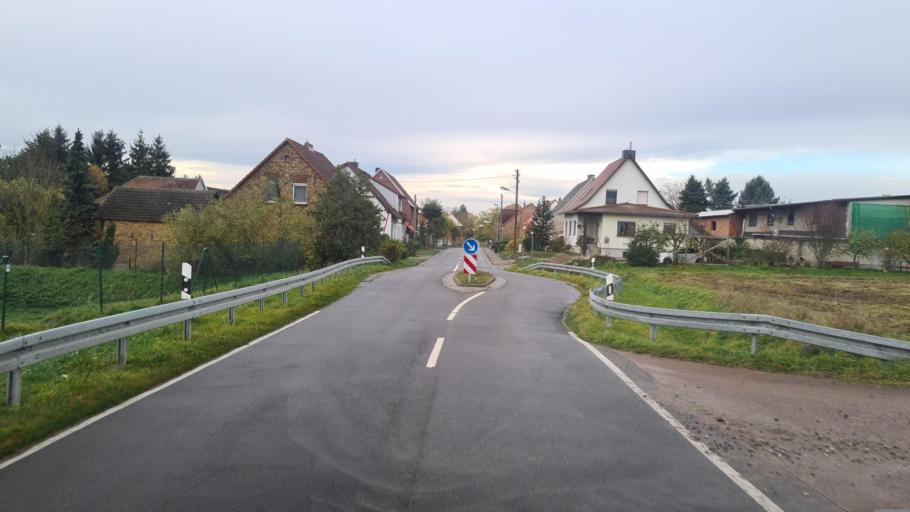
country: DE
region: Saxony-Anhalt
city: Nudersdorf
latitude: 51.9275
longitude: 12.6340
